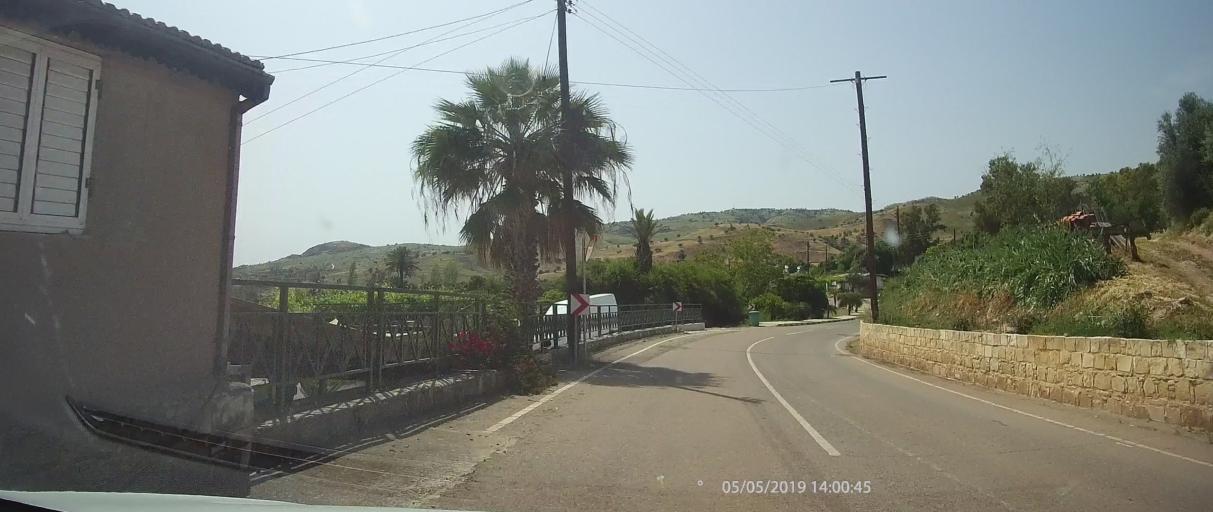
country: CY
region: Limassol
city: Pissouri
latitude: 34.7778
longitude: 32.6551
